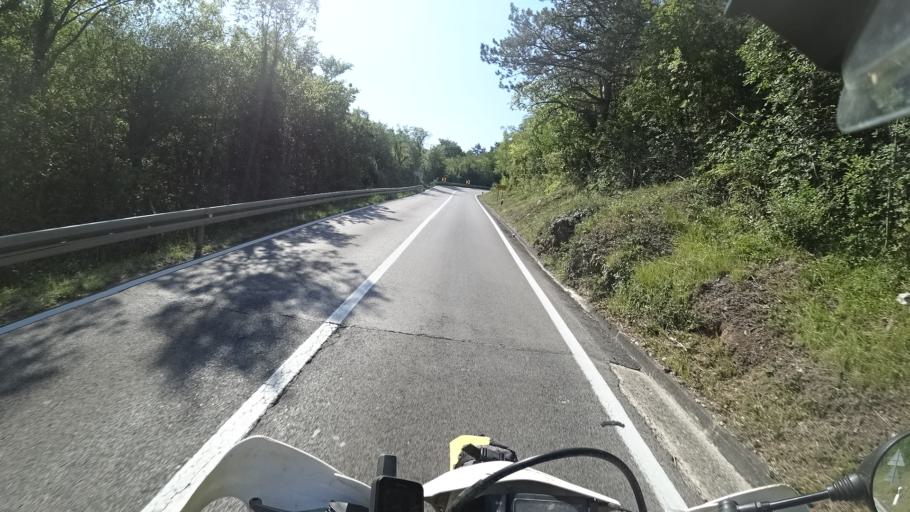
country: HR
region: Sibensko-Kniniska
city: Knin
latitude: 44.0175
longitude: 16.1955
